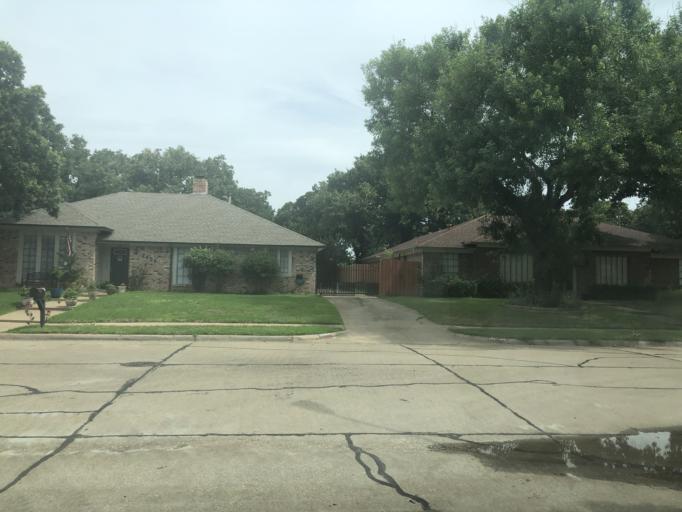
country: US
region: Texas
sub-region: Dallas County
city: Irving
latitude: 32.7987
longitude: -96.9835
